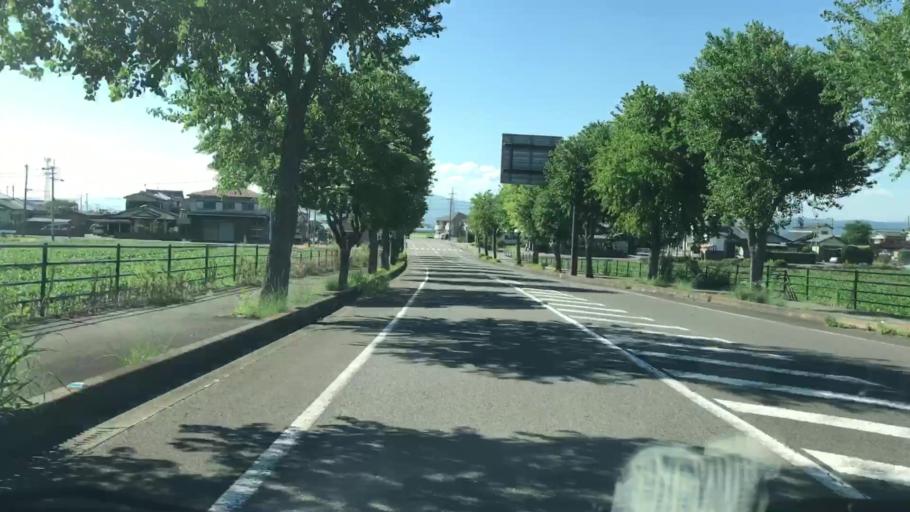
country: JP
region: Saga Prefecture
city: Okawa
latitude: 33.2291
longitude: 130.3689
